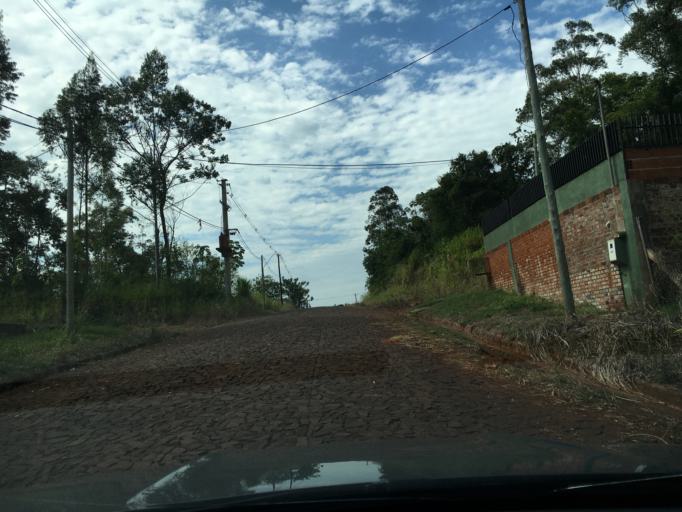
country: AR
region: Misiones
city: Puerto Rico
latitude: -26.7993
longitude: -55.0334
